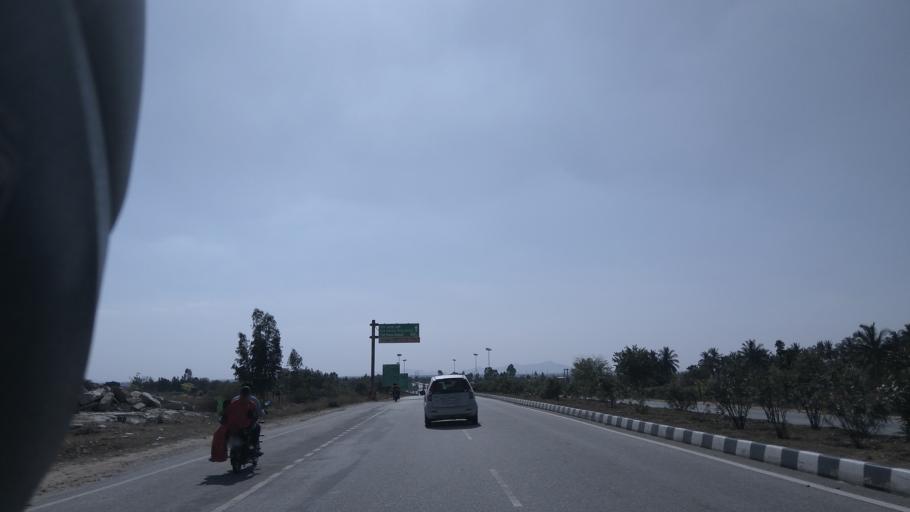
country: IN
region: Karnataka
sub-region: Kolar
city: Mulbagal
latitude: 13.1495
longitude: 78.2963
